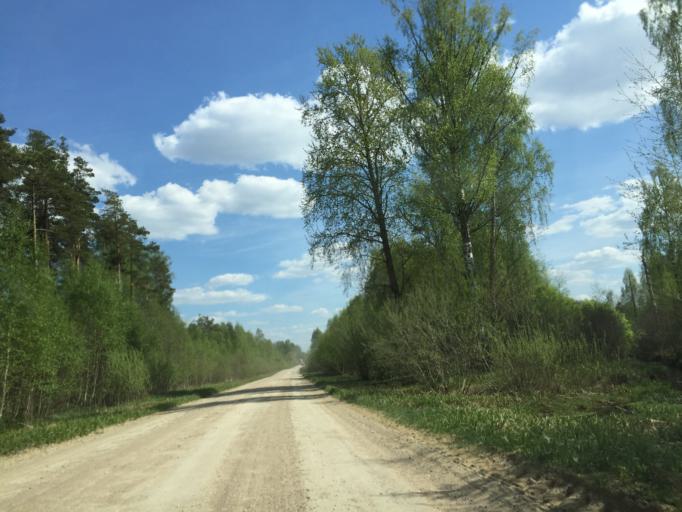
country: LV
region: Limbazu Rajons
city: Limbazi
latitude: 57.3831
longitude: 24.6756
